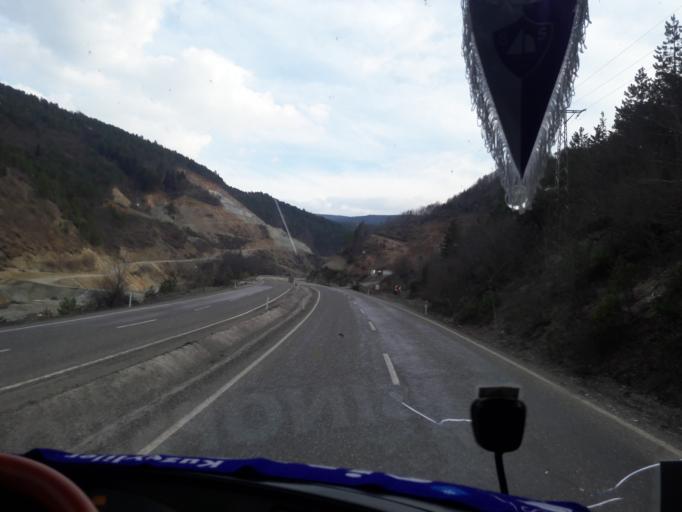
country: TR
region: Kastamonu
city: Kuzyaka
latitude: 41.1877
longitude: 33.7947
